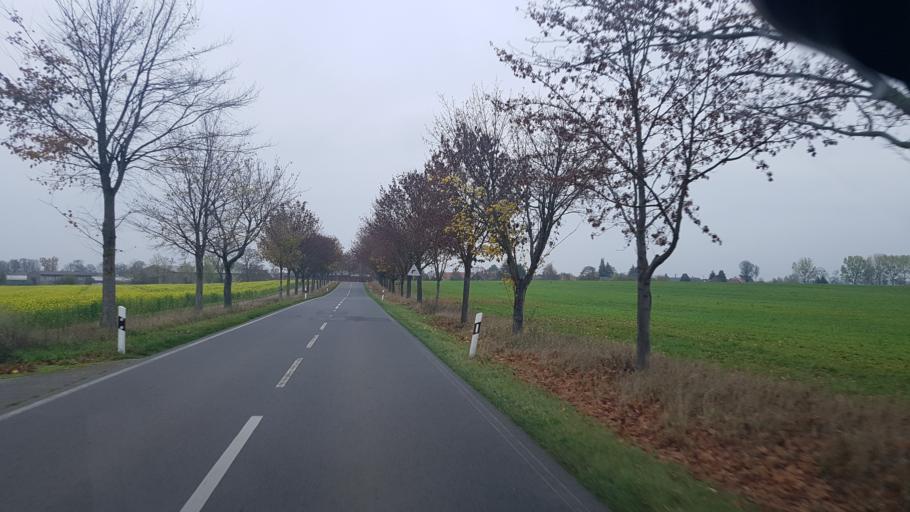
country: DE
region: Brandenburg
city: Schonermark
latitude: 52.9267
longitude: 13.1157
